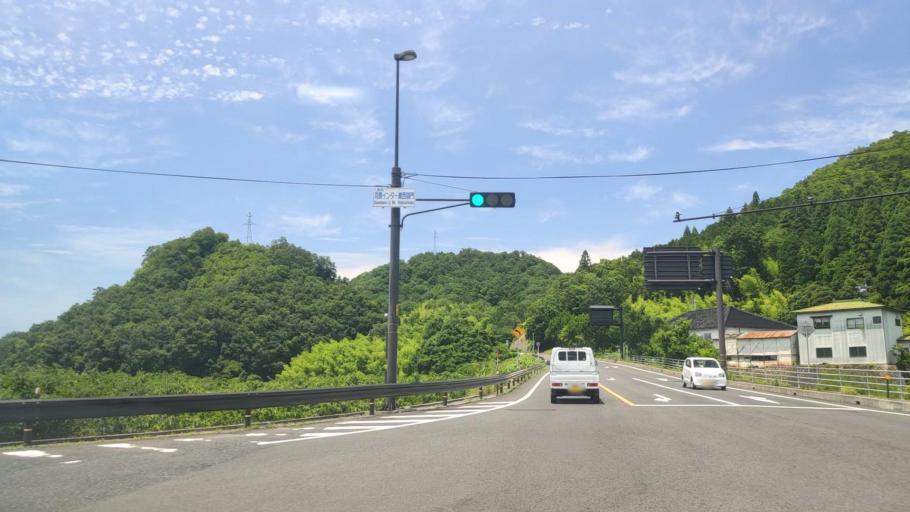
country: JP
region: Tottori
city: Tottori
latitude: 35.3983
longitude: 134.2684
